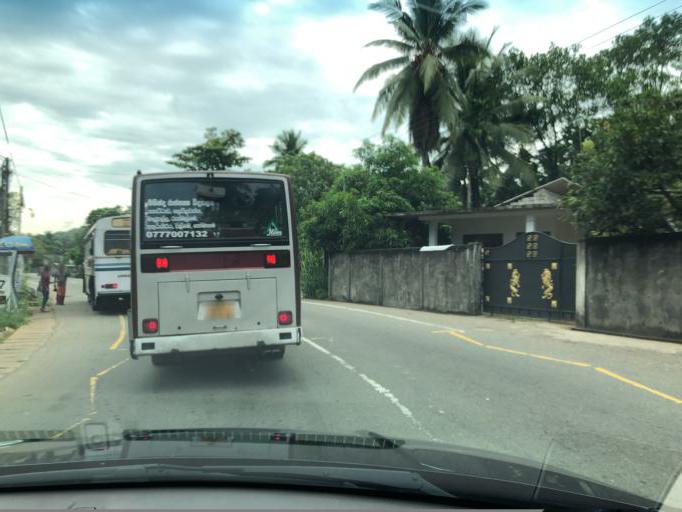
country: LK
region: Western
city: Beruwala
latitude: 6.5420
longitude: 80.0402
